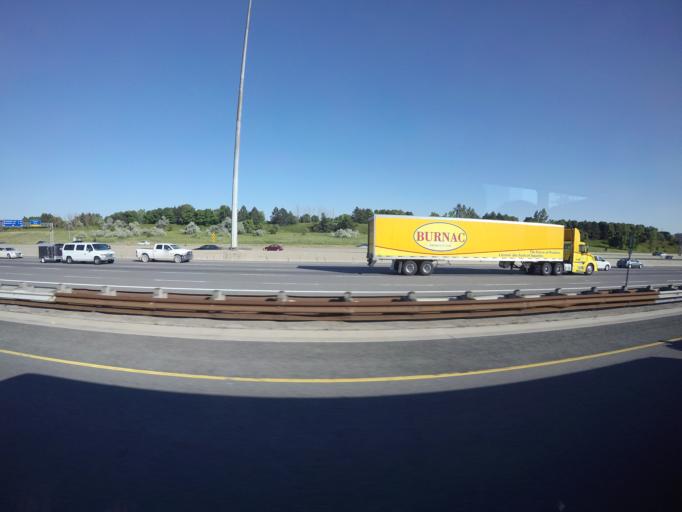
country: CA
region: Ontario
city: Scarborough
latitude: 43.7916
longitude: -79.2219
